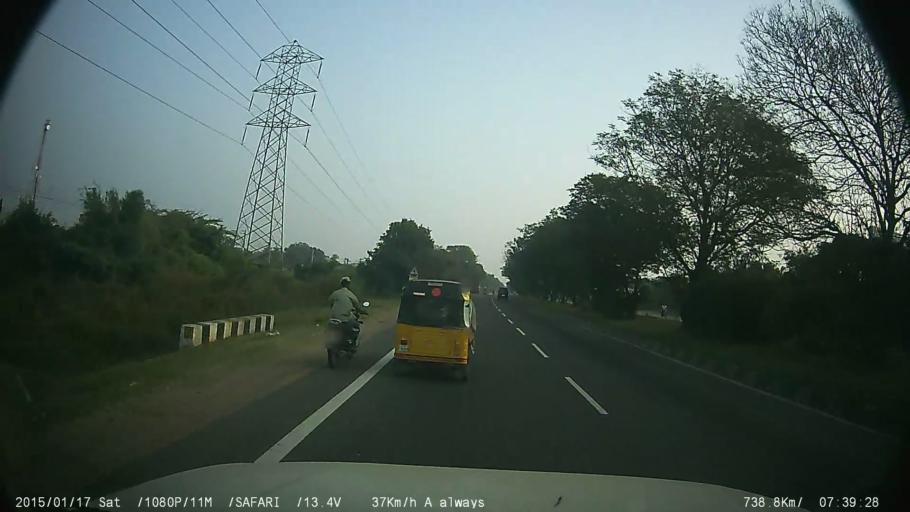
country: IN
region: Tamil Nadu
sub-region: Kancheepuram
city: Singapperumalkovil
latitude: 12.7843
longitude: 80.0135
